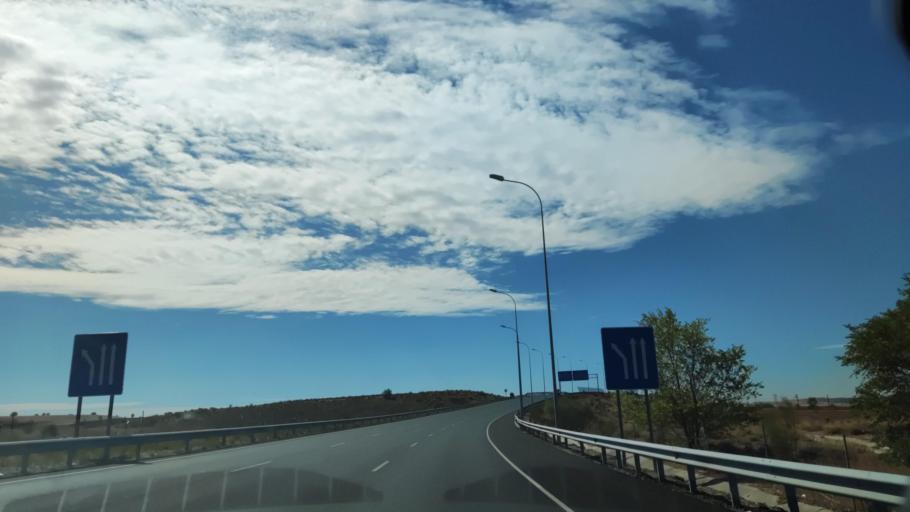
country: ES
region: Madrid
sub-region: Provincia de Madrid
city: Villa de Vallecas
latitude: 40.3376
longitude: -3.6291
